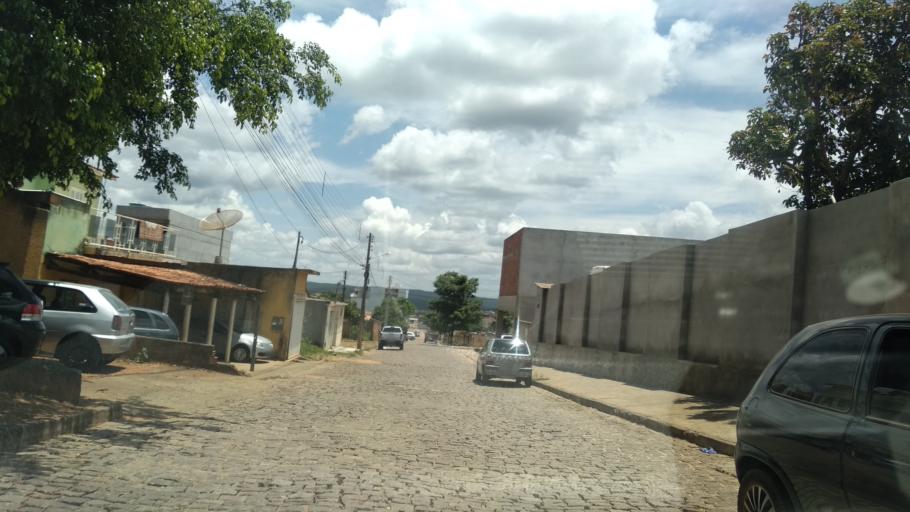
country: BR
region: Bahia
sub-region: Caetite
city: Caetite
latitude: -14.0615
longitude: -42.4861
